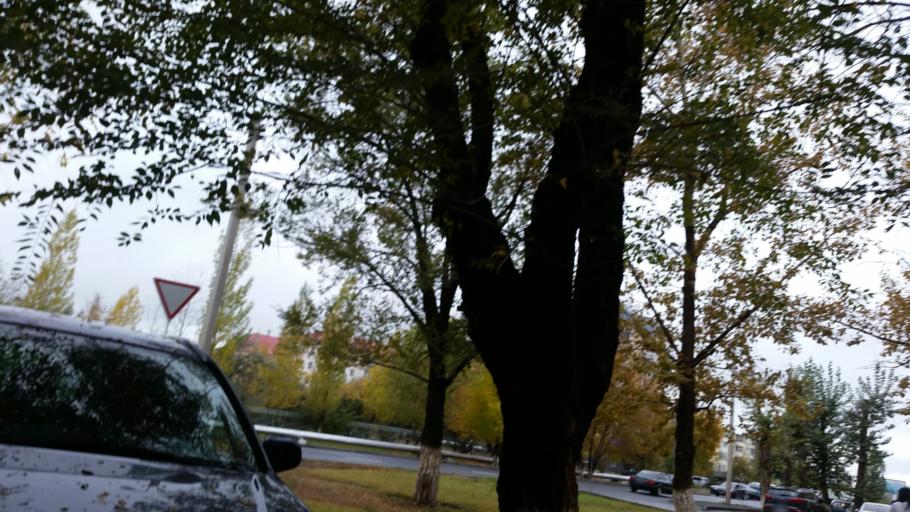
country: KZ
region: Astana Qalasy
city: Astana
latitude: 51.1503
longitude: 71.4631
